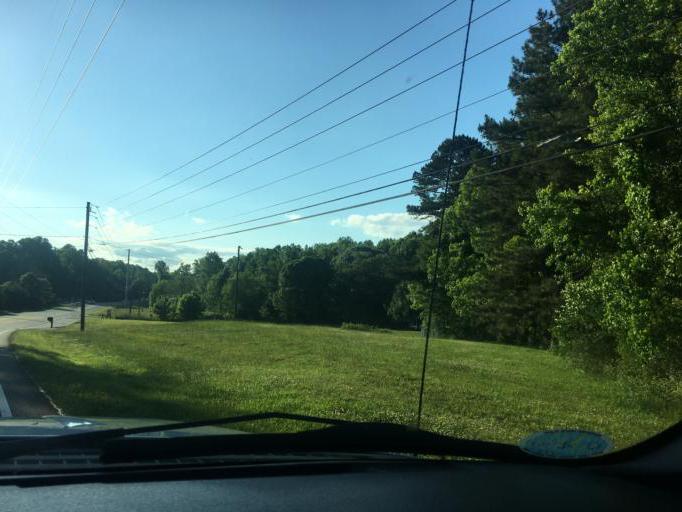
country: US
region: Georgia
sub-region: Forsyth County
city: Cumming
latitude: 34.2745
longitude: -84.1116
